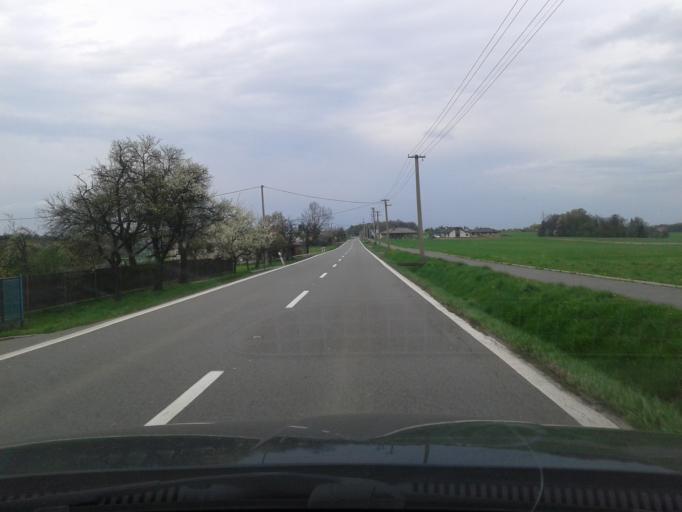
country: CZ
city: Sedliste
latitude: 49.7234
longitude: 18.3678
